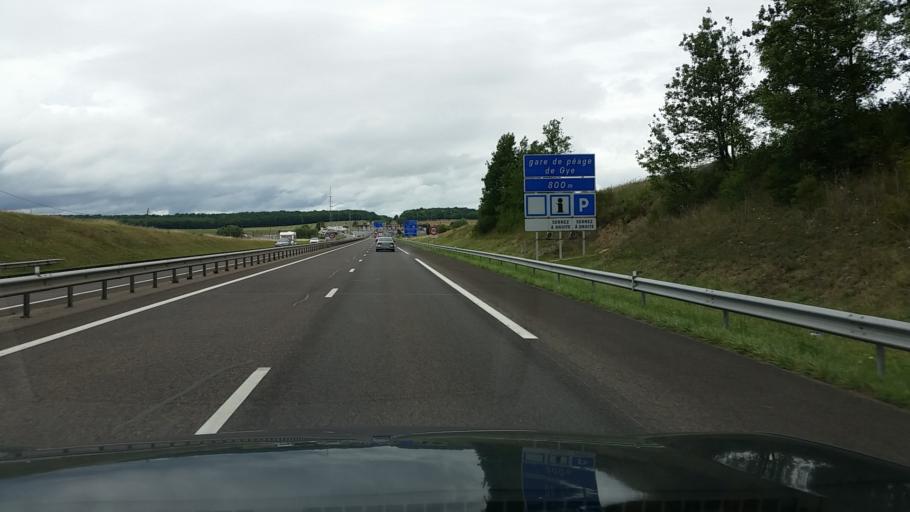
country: FR
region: Lorraine
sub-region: Departement de Meurthe-et-Moselle
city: Blenod-les-Toul
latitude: 48.6225
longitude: 5.8856
